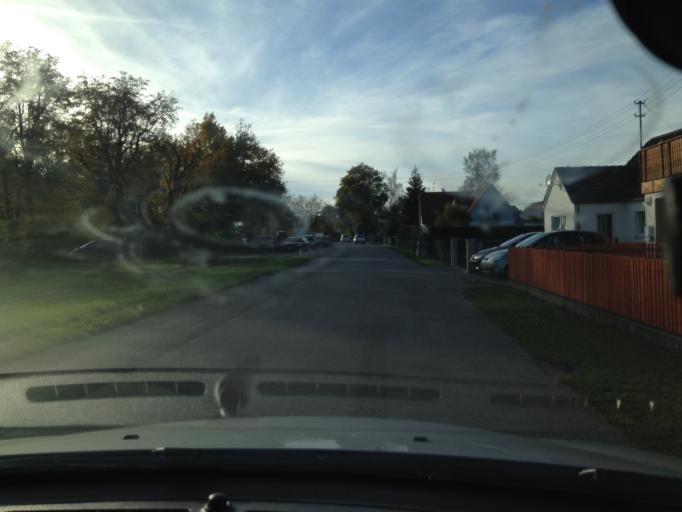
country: DE
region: Bavaria
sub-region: Swabia
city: Konigsbrunn
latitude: 48.2378
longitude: 10.8921
